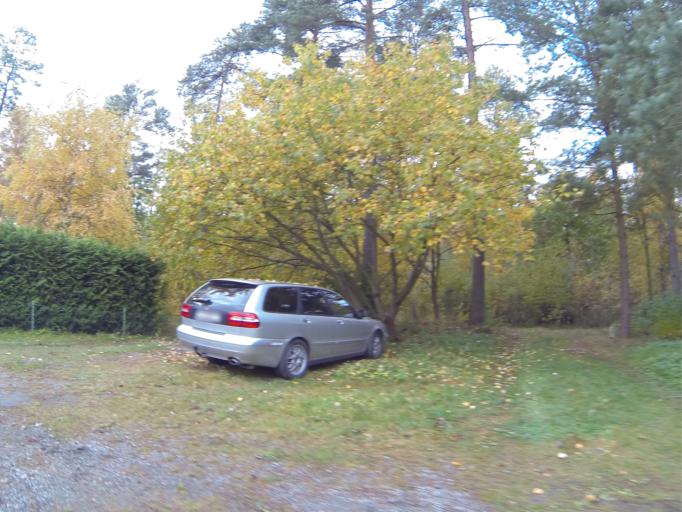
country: SE
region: Skane
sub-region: Sjobo Kommun
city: Blentarp
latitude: 55.6340
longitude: 13.6356
